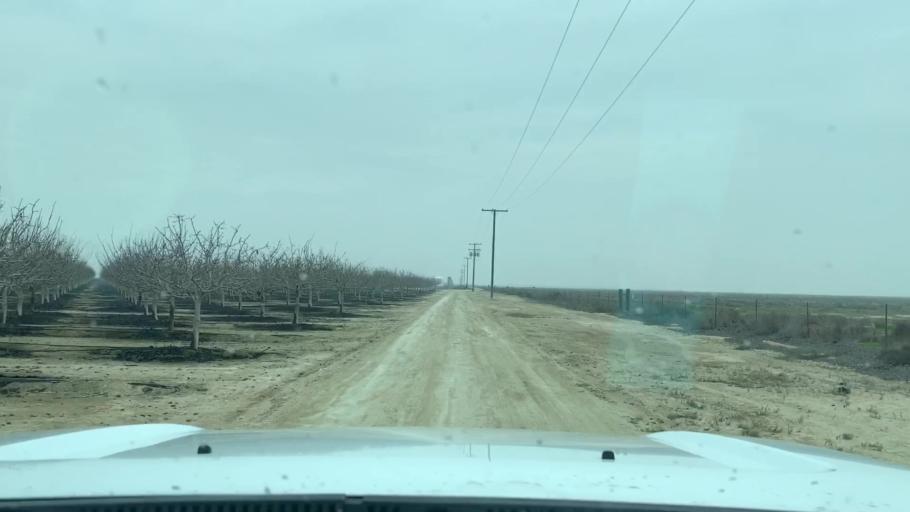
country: US
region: California
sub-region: Tulare County
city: Earlimart
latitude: 35.8387
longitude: -119.3398
